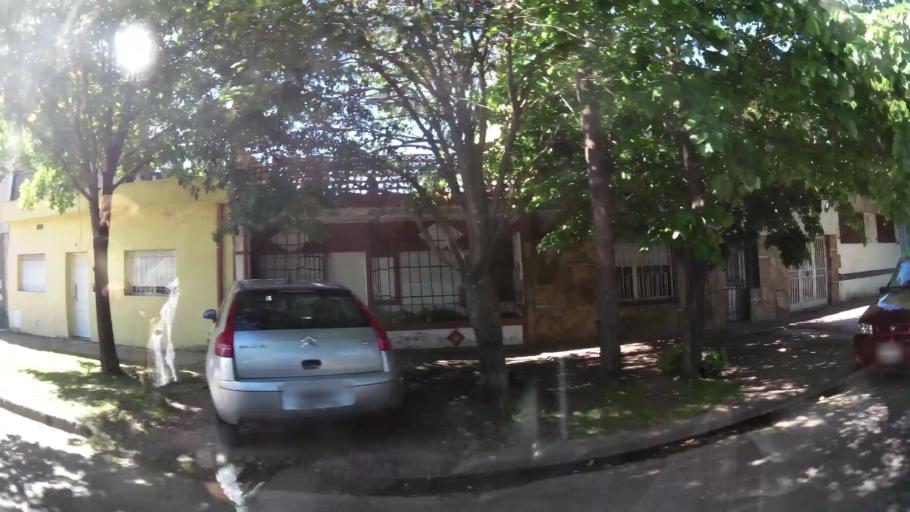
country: AR
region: Santa Fe
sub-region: Departamento de Rosario
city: Rosario
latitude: -32.9355
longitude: -60.7058
